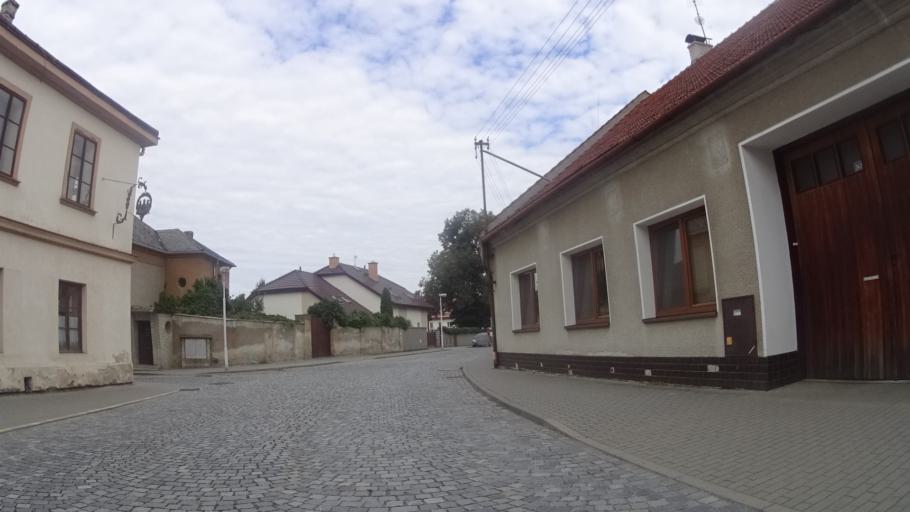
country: CZ
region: Olomoucky
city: Tovacov
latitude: 49.4300
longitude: 17.2890
